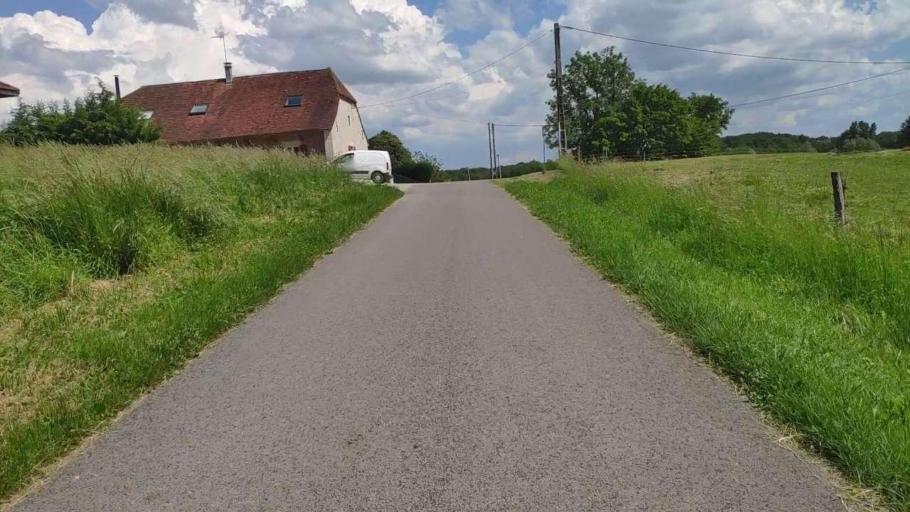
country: FR
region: Franche-Comte
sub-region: Departement du Jura
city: Bletterans
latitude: 46.7813
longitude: 5.4190
